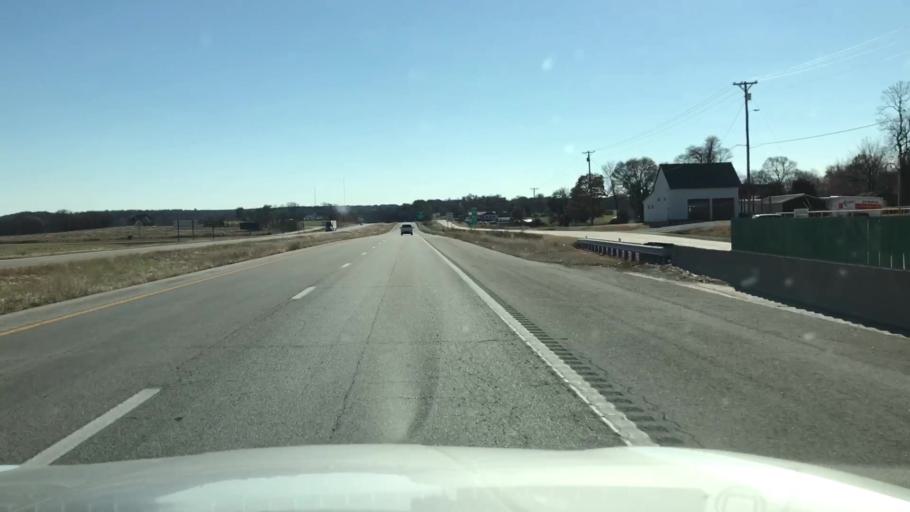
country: US
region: Missouri
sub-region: Jasper County
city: Carthage
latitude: 37.1222
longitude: -94.3112
